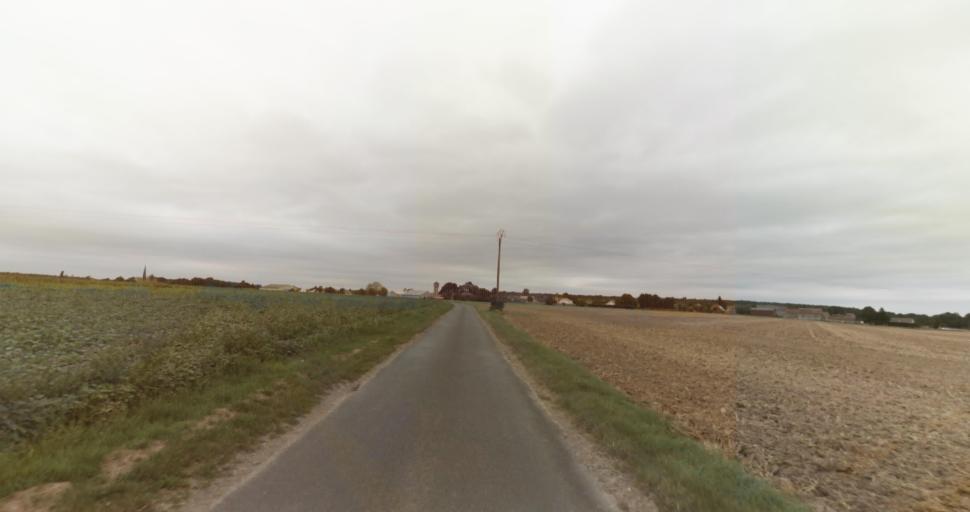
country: FR
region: Haute-Normandie
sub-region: Departement de l'Eure
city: La Couture-Boussey
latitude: 48.9294
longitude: 1.3952
